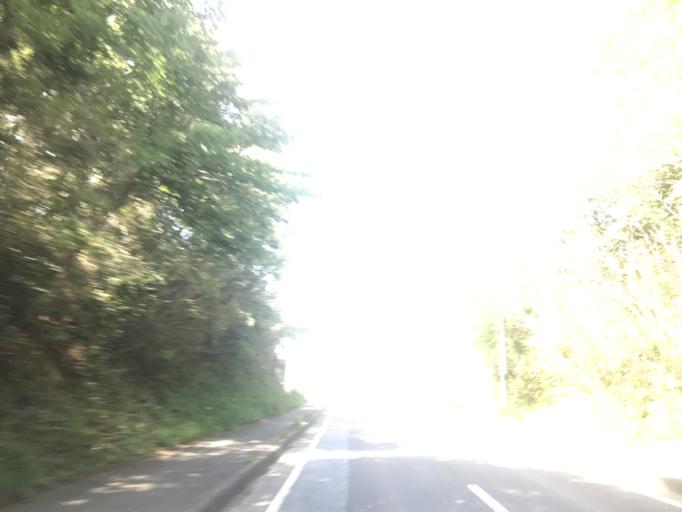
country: JP
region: Chiba
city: Noda
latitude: 35.9599
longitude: 139.9087
